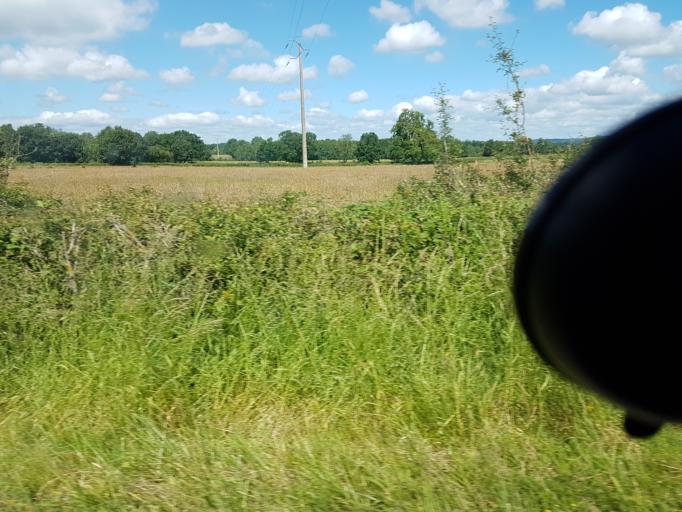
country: FR
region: Bourgogne
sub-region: Departement de Saone-et-Loire
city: Epinac
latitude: 46.9774
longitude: 4.5041
